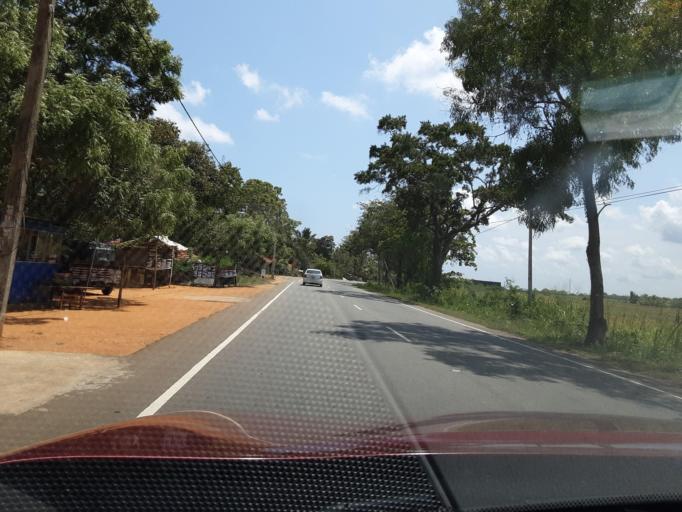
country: LK
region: Southern
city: Tangalla
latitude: 6.2218
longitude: 81.2179
